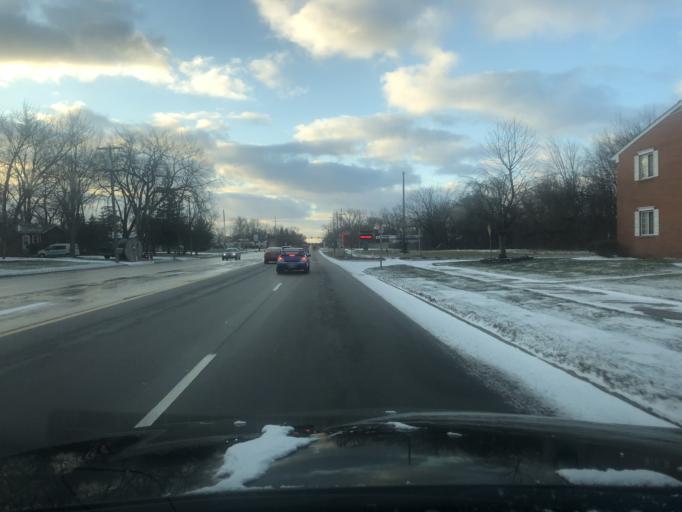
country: US
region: Michigan
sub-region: Wayne County
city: Wayne
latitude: 42.2555
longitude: -83.3479
